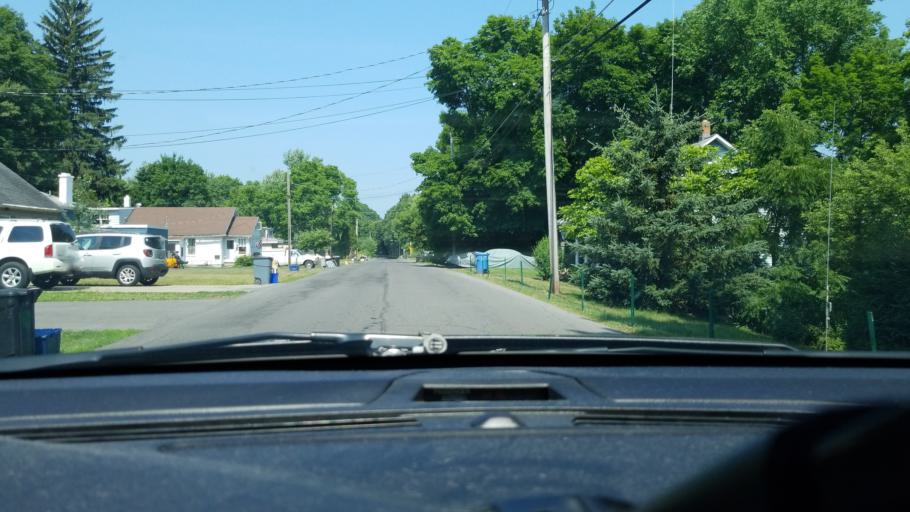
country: US
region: New York
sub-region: Onondaga County
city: Liverpool
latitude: 43.1136
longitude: -76.2157
